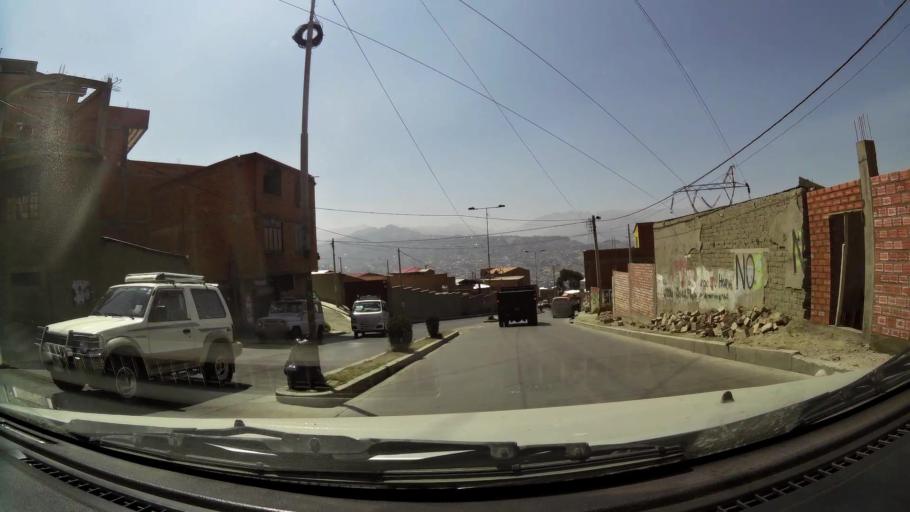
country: BO
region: La Paz
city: La Paz
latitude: -16.5321
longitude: -68.1302
